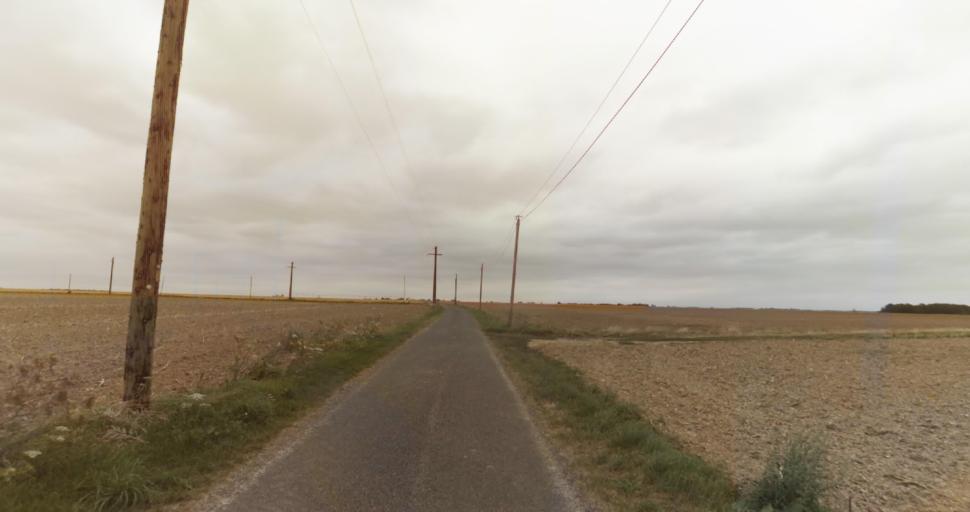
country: FR
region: Haute-Normandie
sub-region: Departement de l'Eure
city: La Couture-Boussey
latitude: 48.9138
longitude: 1.3159
